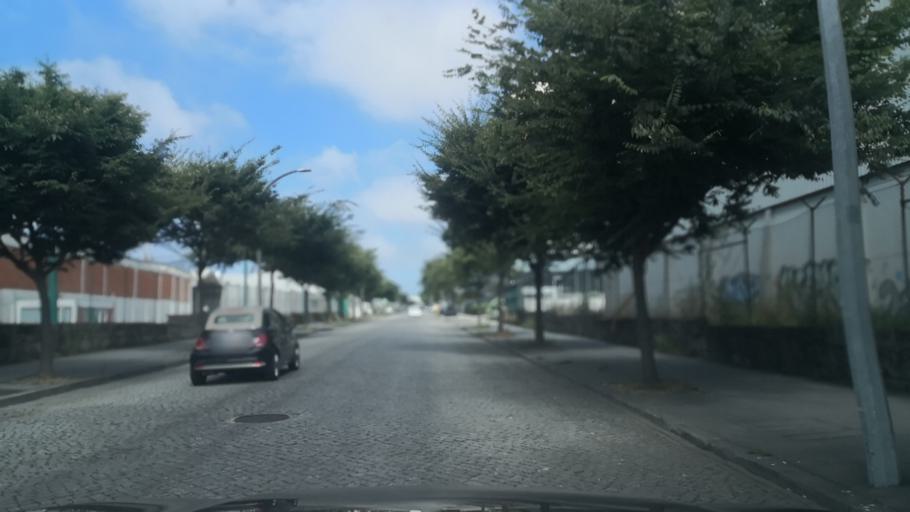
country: PT
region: Porto
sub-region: Matosinhos
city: Senhora da Hora
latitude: 41.1739
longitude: -8.6446
